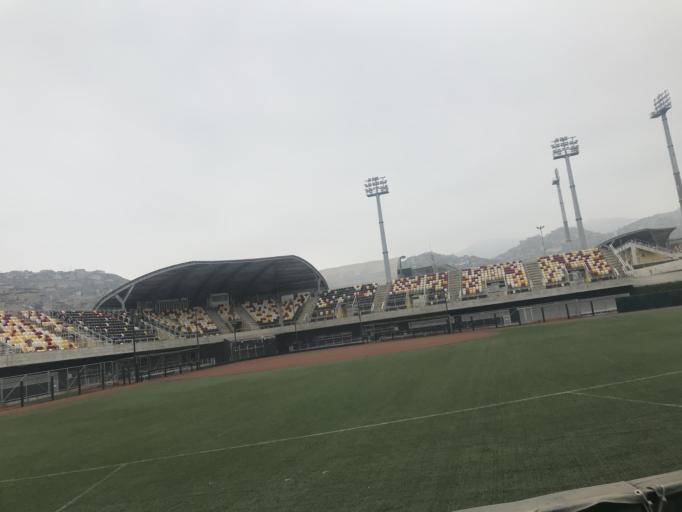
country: PE
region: Lima
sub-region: Lima
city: Surco
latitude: -12.1479
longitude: -76.9527
